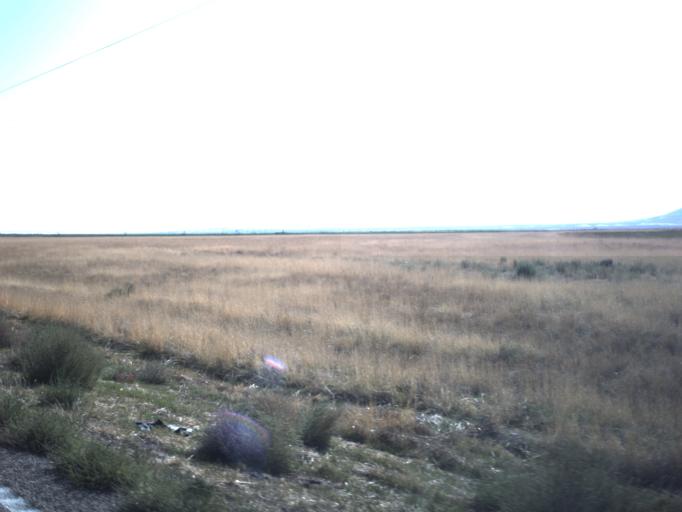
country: US
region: Utah
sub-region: Millard County
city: Delta
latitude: 39.1903
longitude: -112.4100
